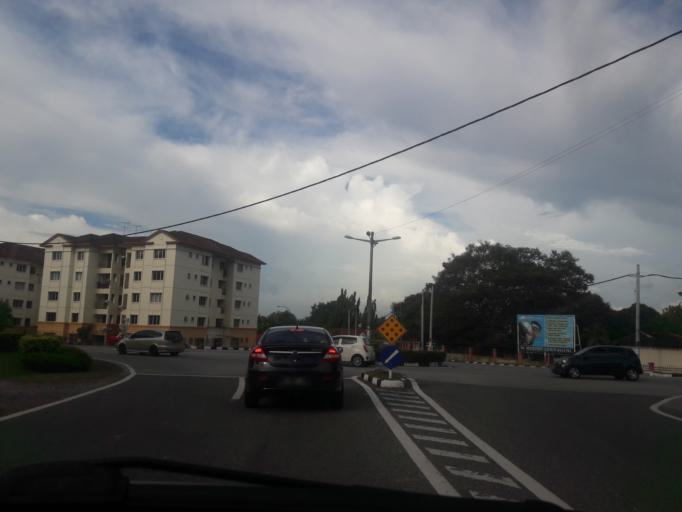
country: MY
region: Kedah
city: Sungai Petani
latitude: 5.6528
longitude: 100.4879
